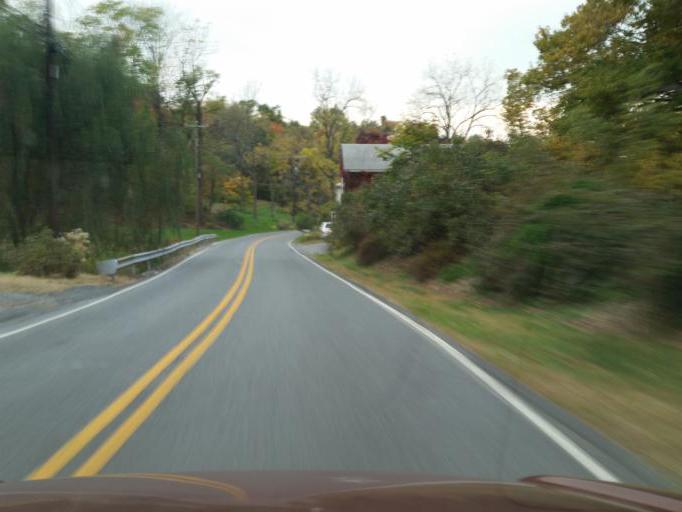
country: US
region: Pennsylvania
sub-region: Dauphin County
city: Hummelstown
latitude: 40.2359
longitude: -76.7004
